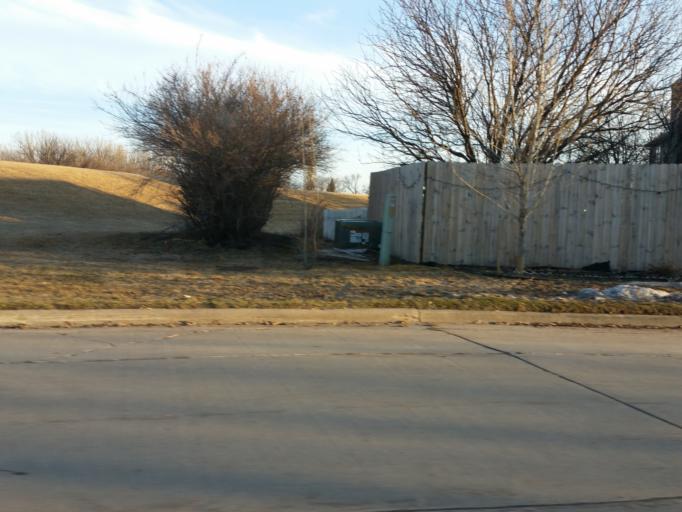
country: US
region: North Dakota
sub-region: Grand Forks County
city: Grand Forks
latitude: 47.8756
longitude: -97.0254
